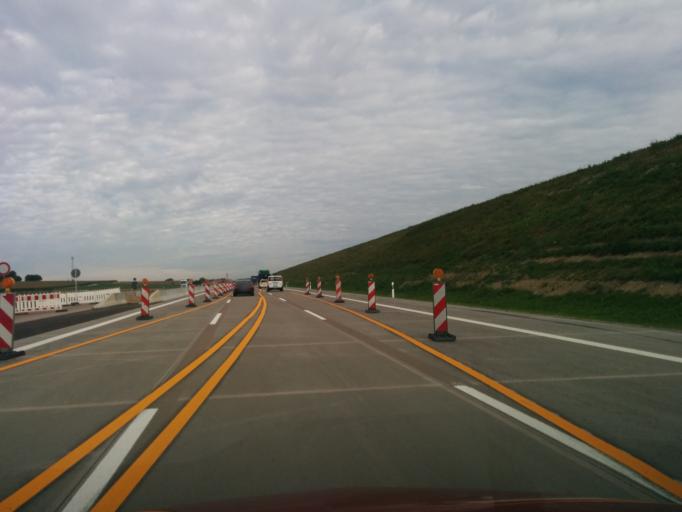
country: DE
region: Bavaria
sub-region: Swabia
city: Burgau
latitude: 48.4179
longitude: 10.3998
